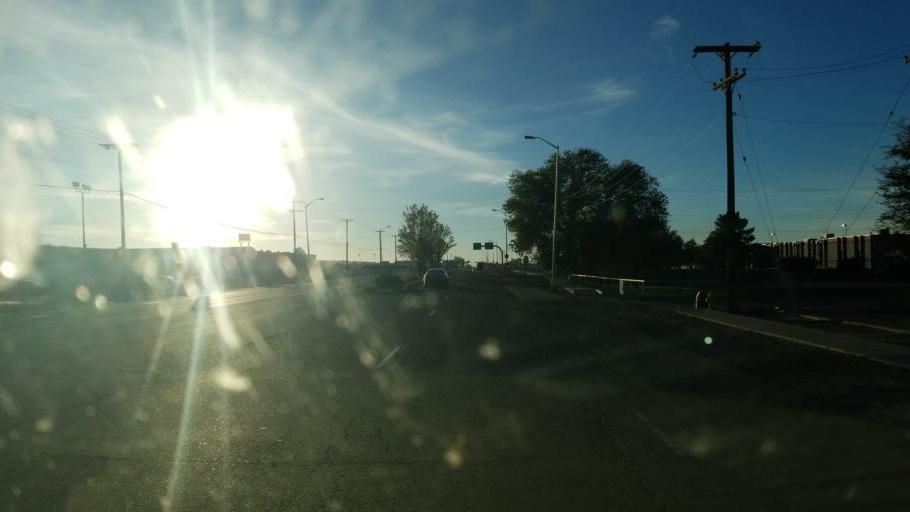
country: US
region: New Mexico
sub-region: San Juan County
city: Farmington
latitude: 36.7194
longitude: -108.1779
